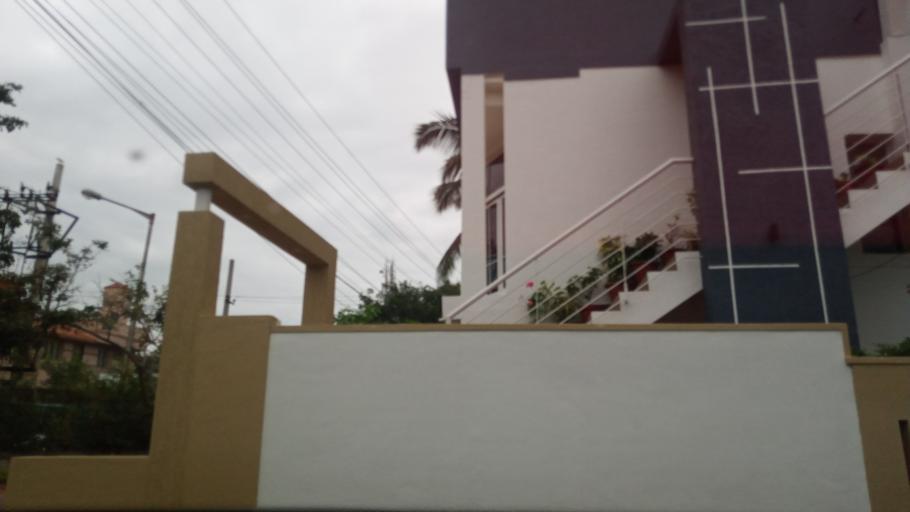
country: IN
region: Karnataka
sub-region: Mysore
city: Mysore
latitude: 12.2895
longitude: 76.6168
